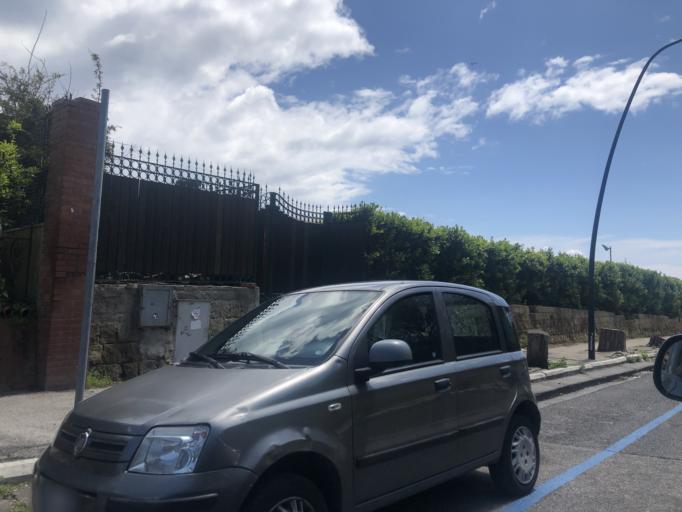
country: IT
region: Campania
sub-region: Provincia di Napoli
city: Bagnoli
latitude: 40.7991
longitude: 14.1817
